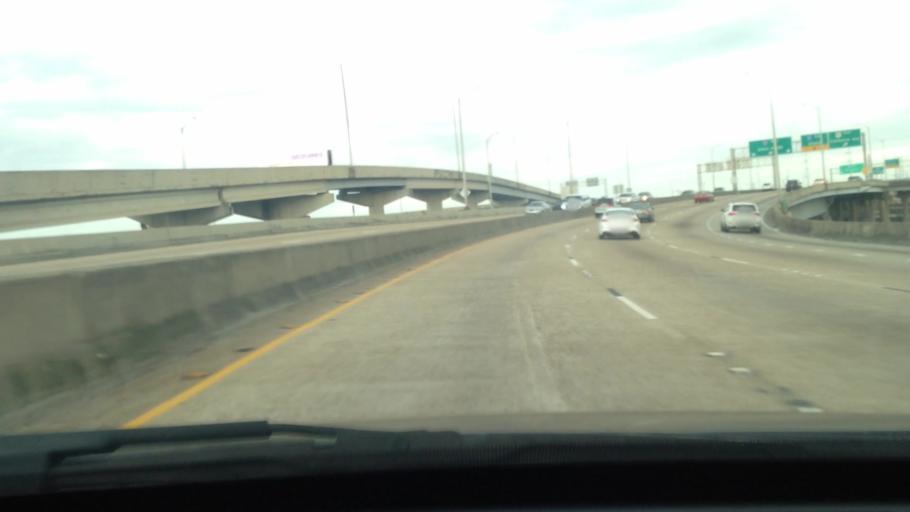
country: US
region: Louisiana
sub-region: Orleans Parish
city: New Orleans
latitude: 29.9484
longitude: -90.0837
